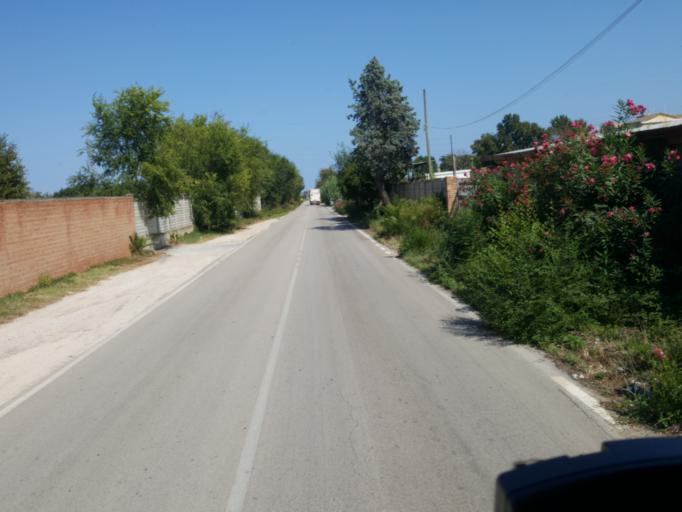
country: IT
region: Abruzzo
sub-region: Provincia di Chieti
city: Salvo Marina
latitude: 42.0580
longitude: 14.7571
